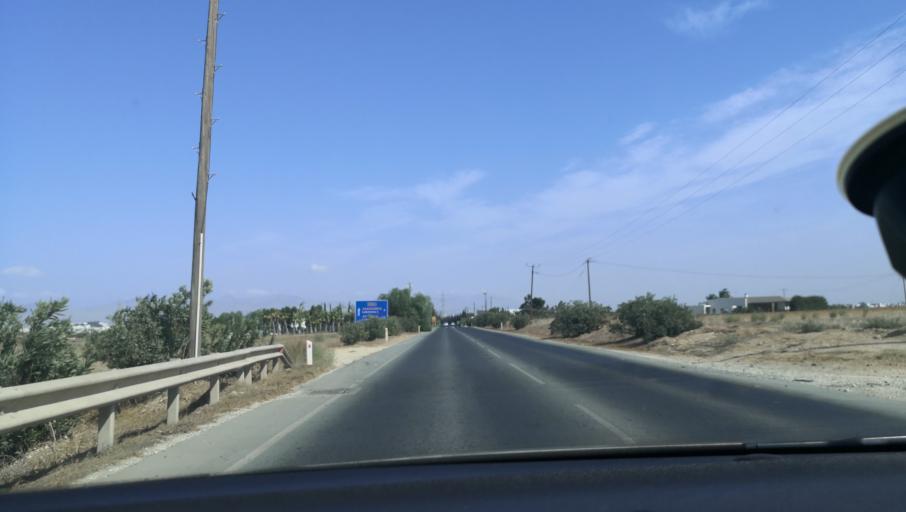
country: CY
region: Lefkosia
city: Kato Deftera
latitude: 35.0942
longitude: 33.2825
